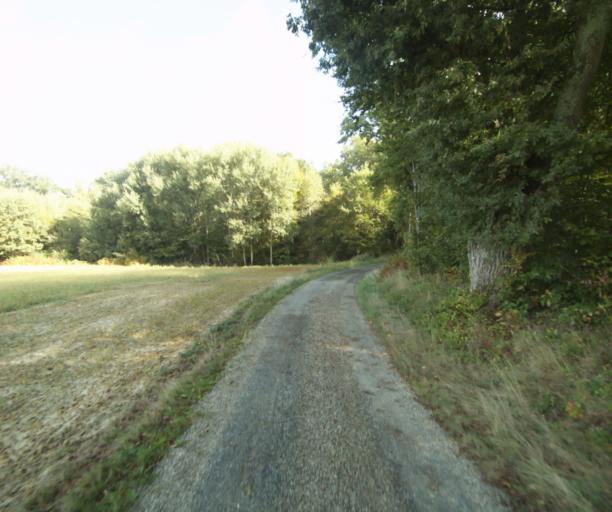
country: FR
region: Midi-Pyrenees
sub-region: Departement du Gers
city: Nogaro
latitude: 43.8380
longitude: -0.0530
